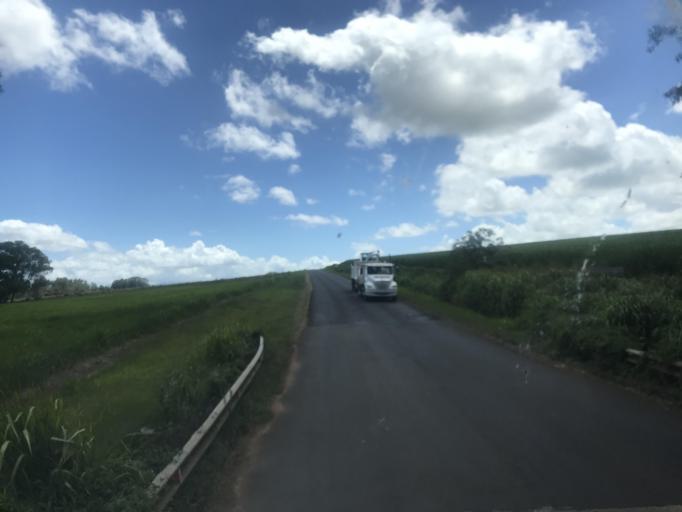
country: AU
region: Queensland
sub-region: Tablelands
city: Tolga
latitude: -17.2367
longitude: 145.5050
